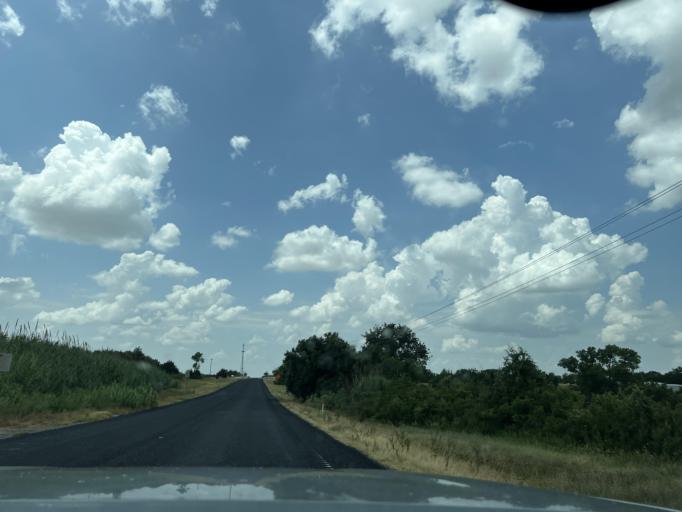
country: US
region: Texas
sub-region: Wise County
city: Boyd
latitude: 33.0742
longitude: -97.6498
